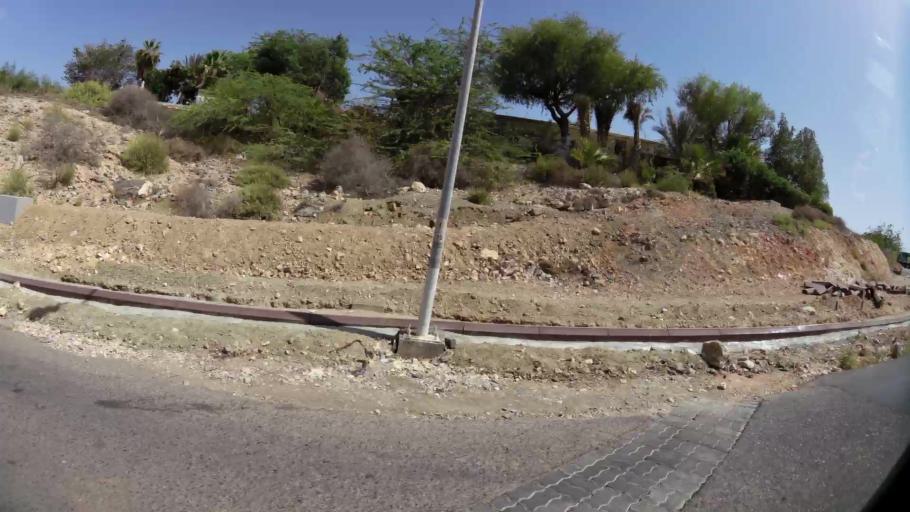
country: OM
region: Muhafazat Masqat
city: Muscat
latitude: 23.6359
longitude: 58.4906
